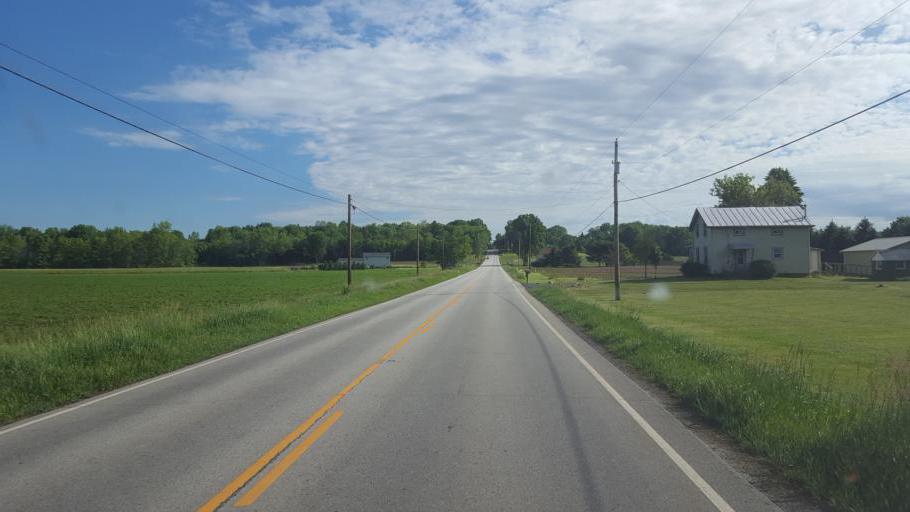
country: US
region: Ohio
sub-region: Wayne County
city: Creston
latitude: 40.9957
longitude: -81.8893
